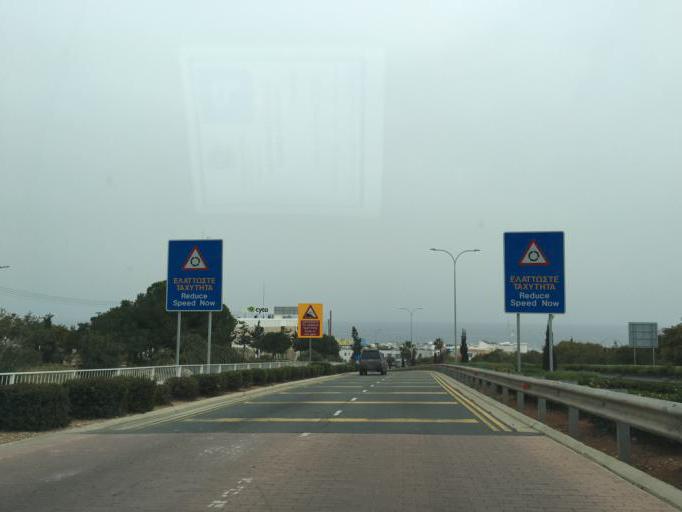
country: CY
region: Ammochostos
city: Ayia Napa
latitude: 34.9959
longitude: 34.0006
